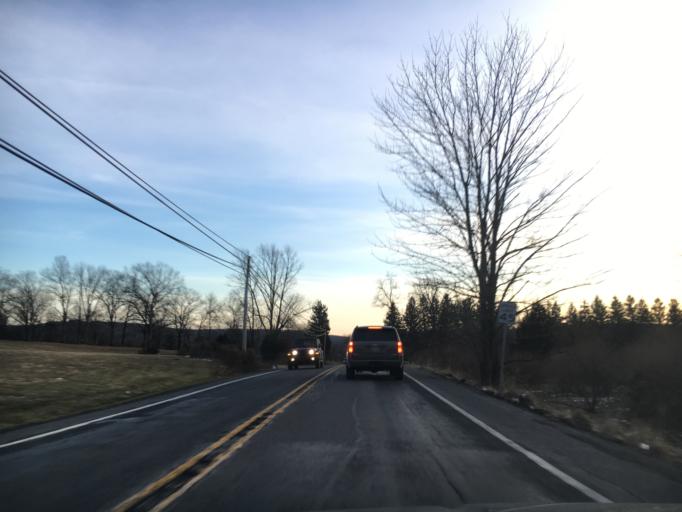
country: US
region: Pennsylvania
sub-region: Monroe County
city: East Stroudsburg
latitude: 41.0496
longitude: -75.1284
